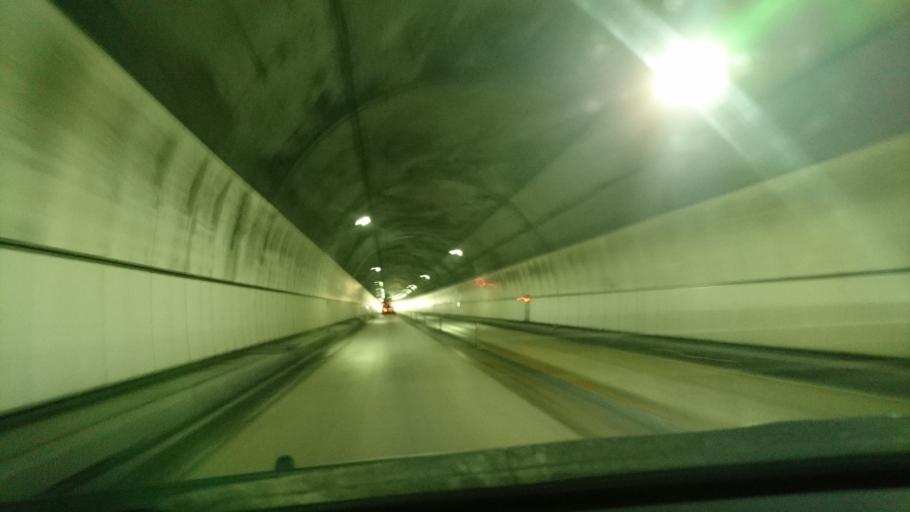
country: JP
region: Aomori
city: Hachinohe
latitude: 40.2038
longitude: 141.7840
